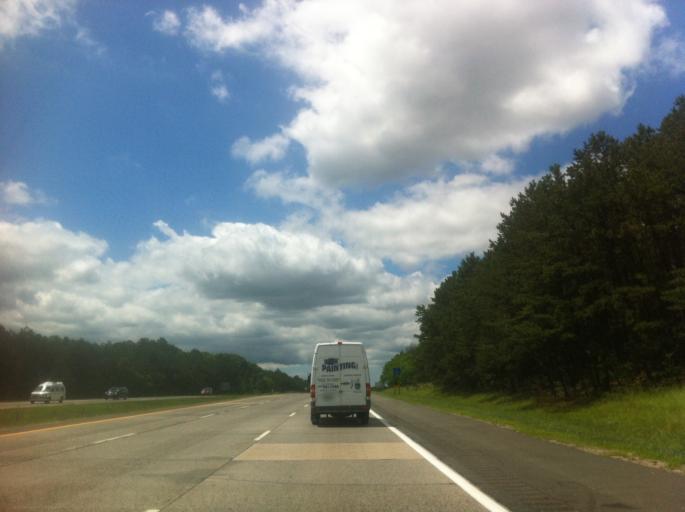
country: US
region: New York
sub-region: Suffolk County
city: Calverton
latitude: 40.8972
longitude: -72.7461
